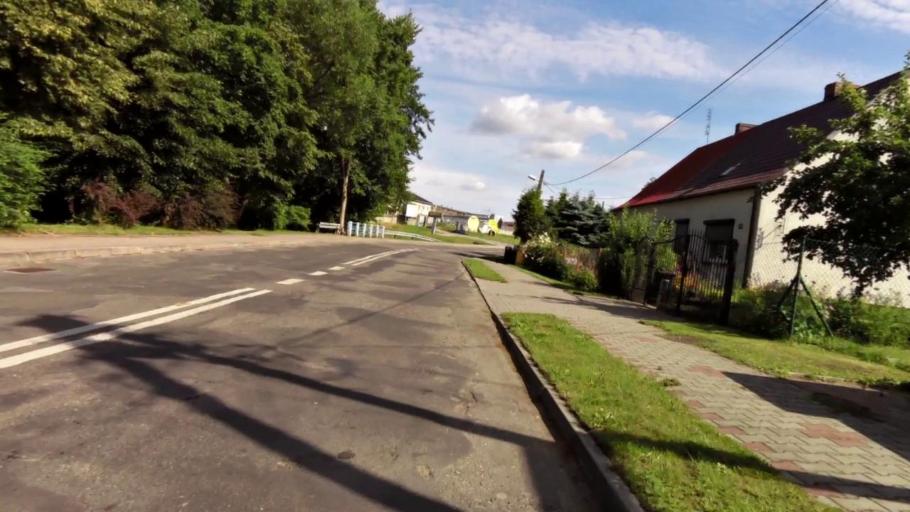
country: PL
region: West Pomeranian Voivodeship
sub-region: Powiat stargardzki
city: Dobrzany
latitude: 53.3645
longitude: 15.4282
